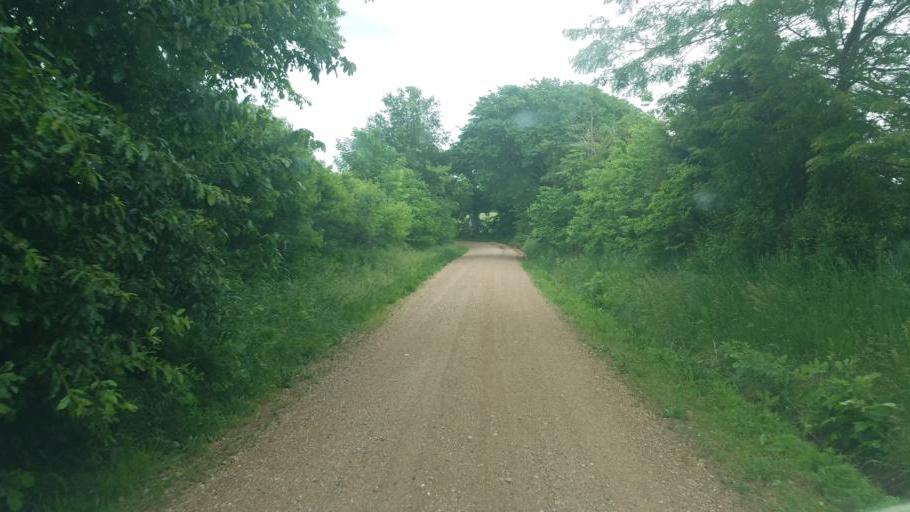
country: US
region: Missouri
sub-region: Moniteau County
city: California
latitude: 38.5946
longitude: -92.6489
